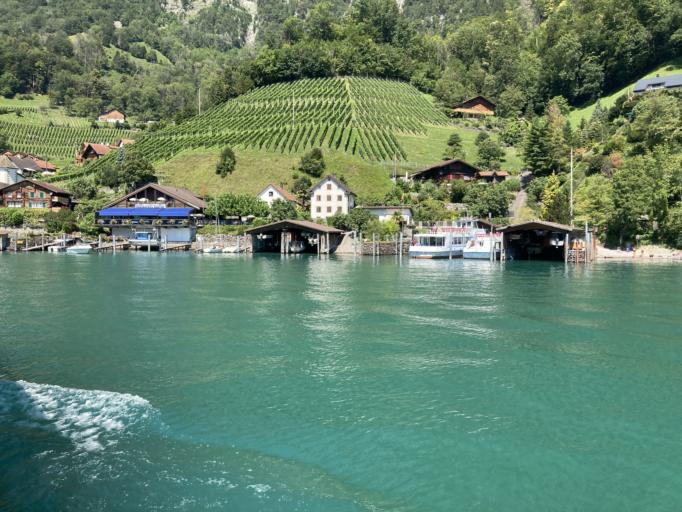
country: CH
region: Saint Gallen
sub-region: Wahlkreis Sarganserland
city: Quarten
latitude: 47.1284
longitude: 9.2178
